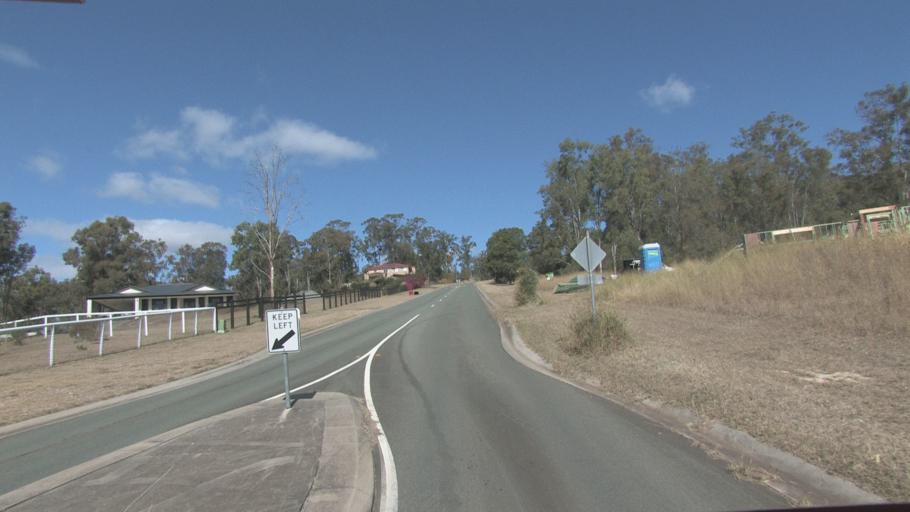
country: AU
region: Queensland
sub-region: Logan
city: Cedar Vale
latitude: -27.8887
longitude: 153.0032
